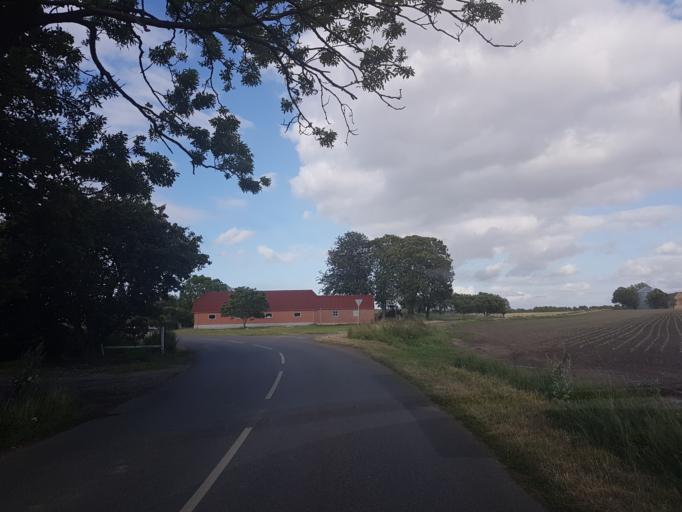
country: DK
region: South Denmark
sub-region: Nordfyns Kommune
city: Bogense
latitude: 55.5472
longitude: 10.0614
